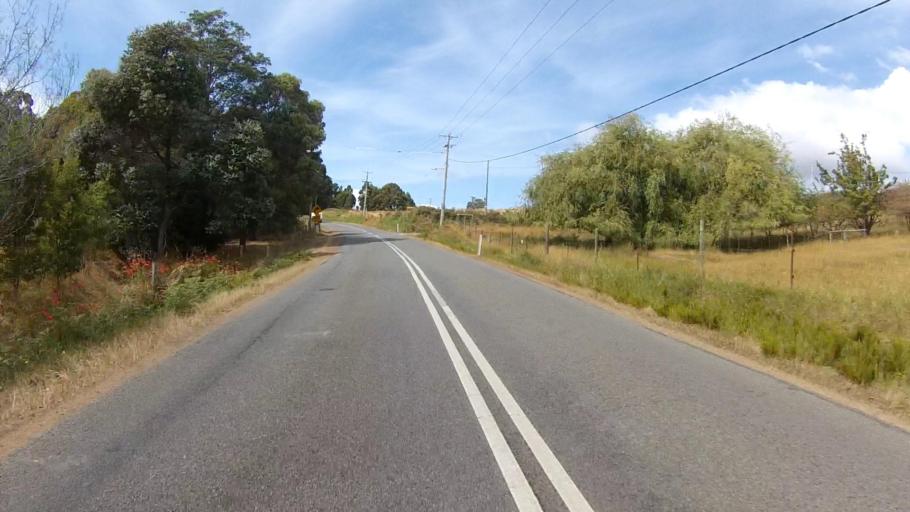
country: AU
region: Tasmania
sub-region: Kingborough
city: Kettering
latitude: -43.2099
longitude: 147.2559
